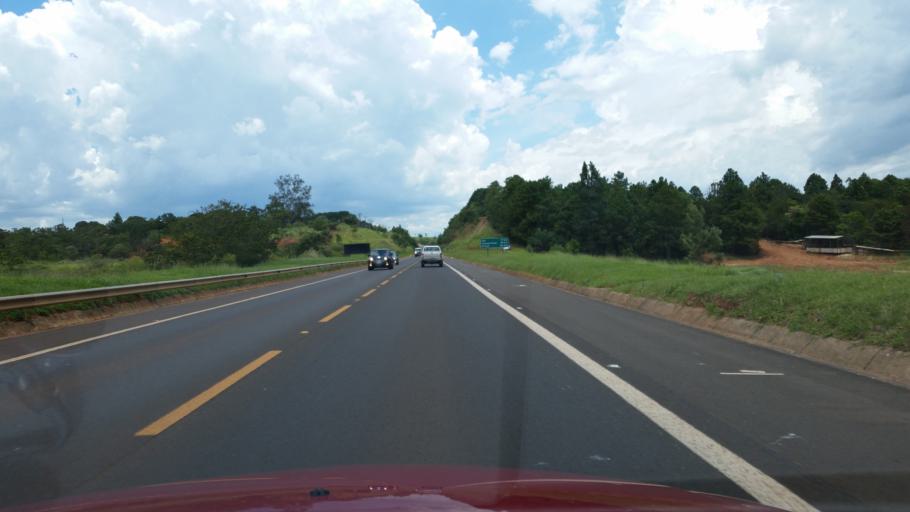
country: BR
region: Sao Paulo
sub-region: Itai
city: Itai
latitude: -23.2729
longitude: -49.0161
